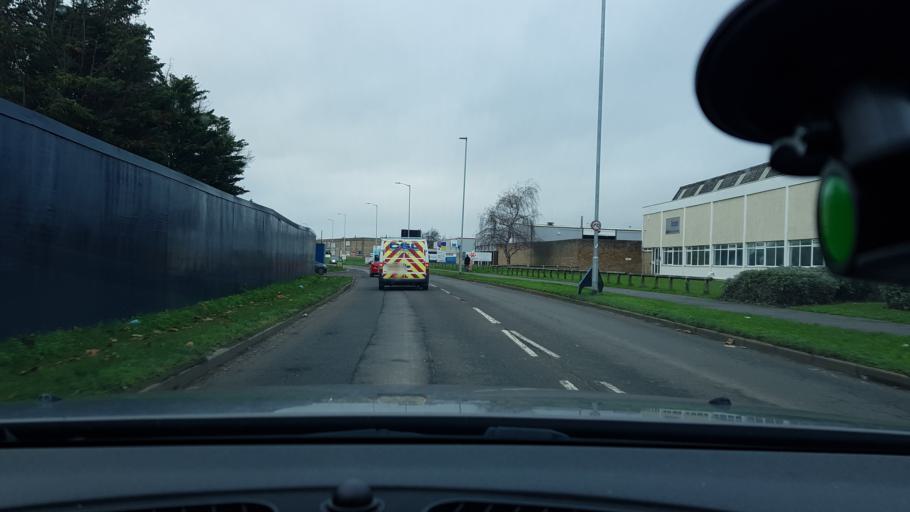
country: GB
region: England
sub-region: Reading
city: Reading
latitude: 51.4600
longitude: -0.9937
